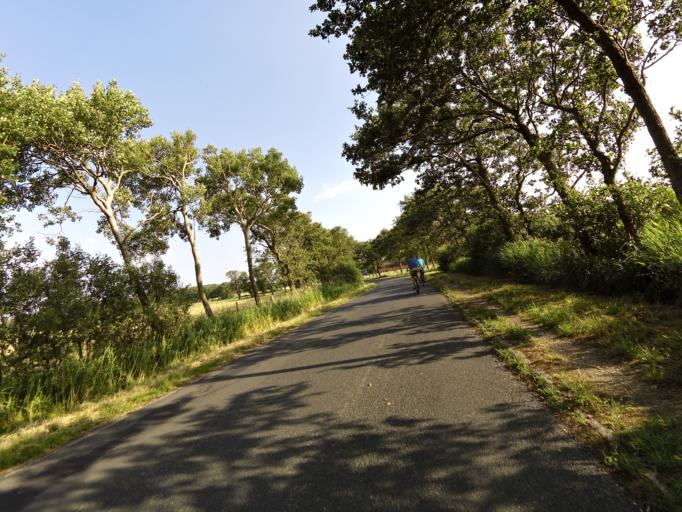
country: DE
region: Lower Saxony
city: Nordholz
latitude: 53.8298
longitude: 8.5813
